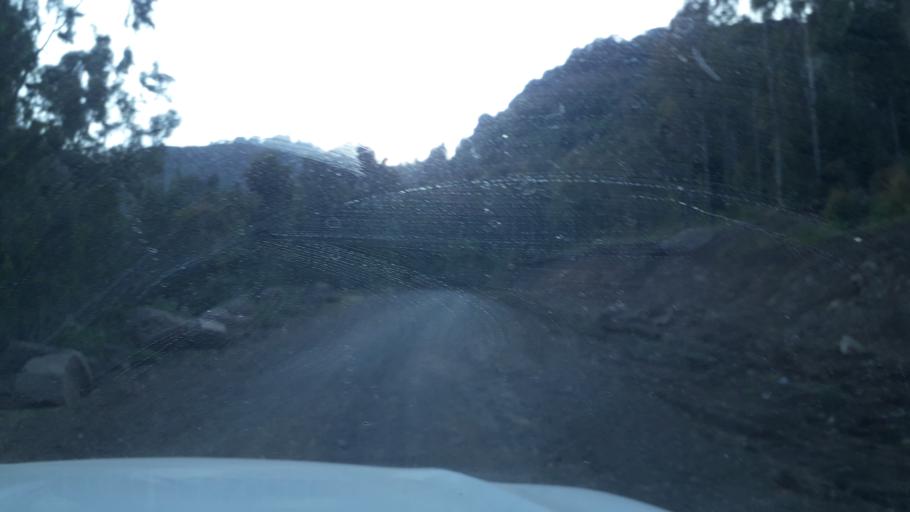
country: ET
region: Amhara
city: Lalibela
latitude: 11.5514
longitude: 39.2160
